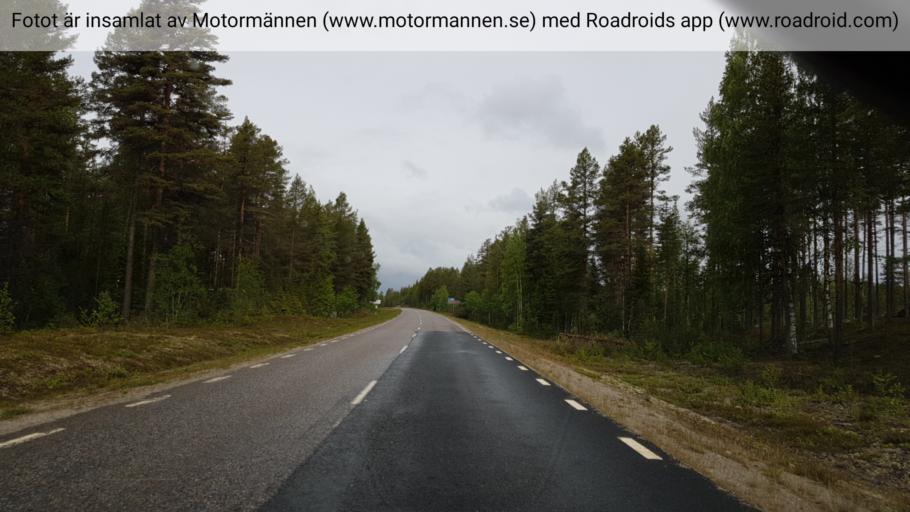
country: SE
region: Vaesterbotten
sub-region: Norsjo Kommun
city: Norsjoe
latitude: 64.6814
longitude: 19.2437
